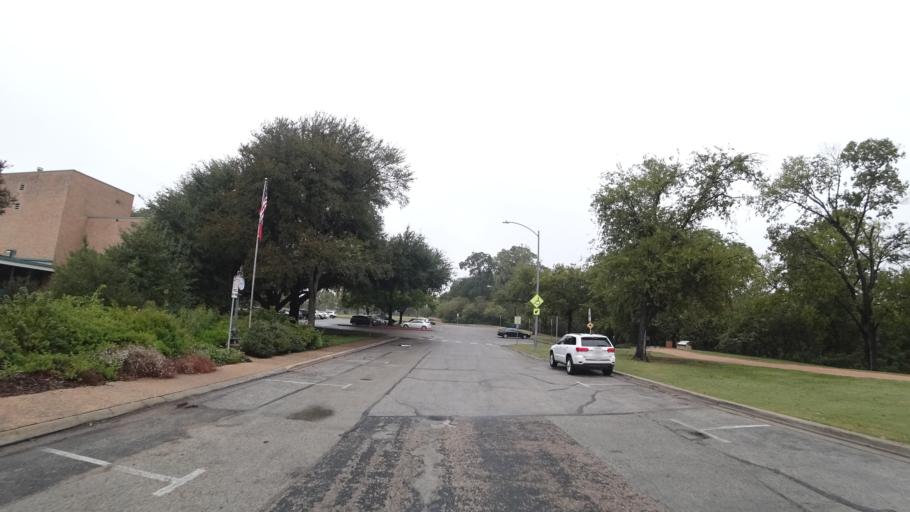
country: US
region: Texas
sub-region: Travis County
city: Austin
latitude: 30.2652
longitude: -97.7583
